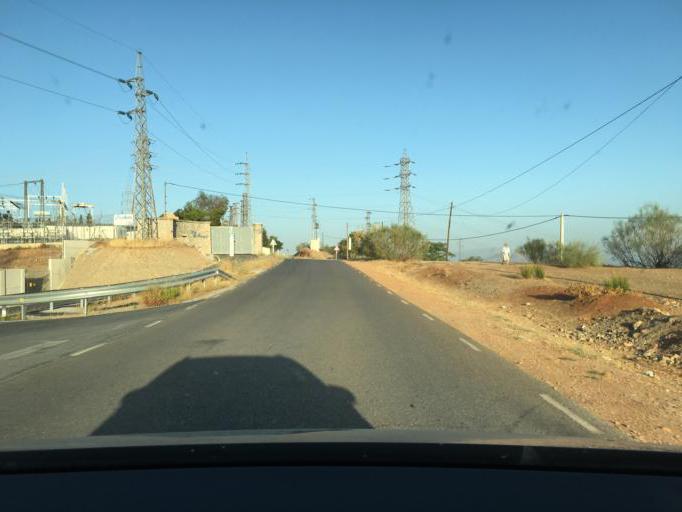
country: ES
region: Andalusia
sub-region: Provincia de Granada
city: Jun
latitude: 37.1970
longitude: -3.5745
